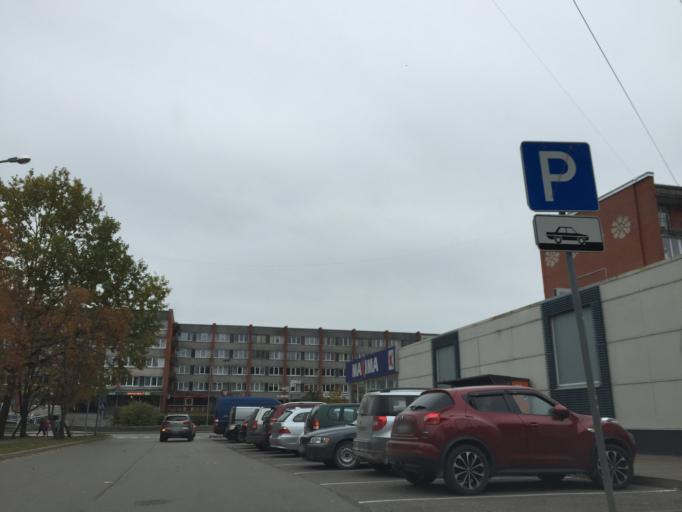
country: LV
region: Olaine
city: Olaine
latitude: 56.7850
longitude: 23.9364
